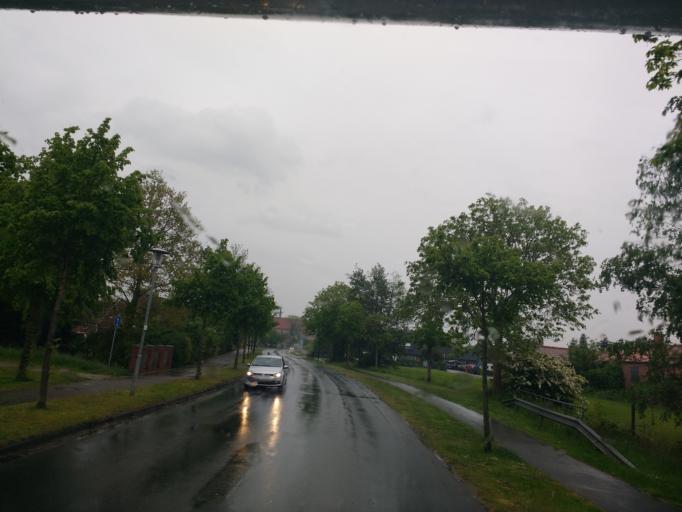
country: DE
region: Lower Saxony
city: Jever
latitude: 53.6658
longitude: 7.9124
